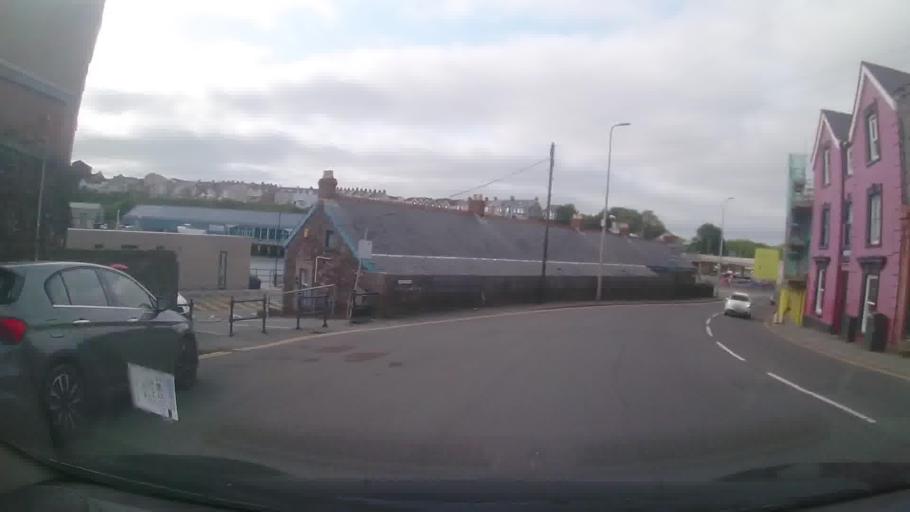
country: GB
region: Wales
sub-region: Pembrokeshire
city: Milford Haven
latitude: 51.7127
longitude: -5.0399
